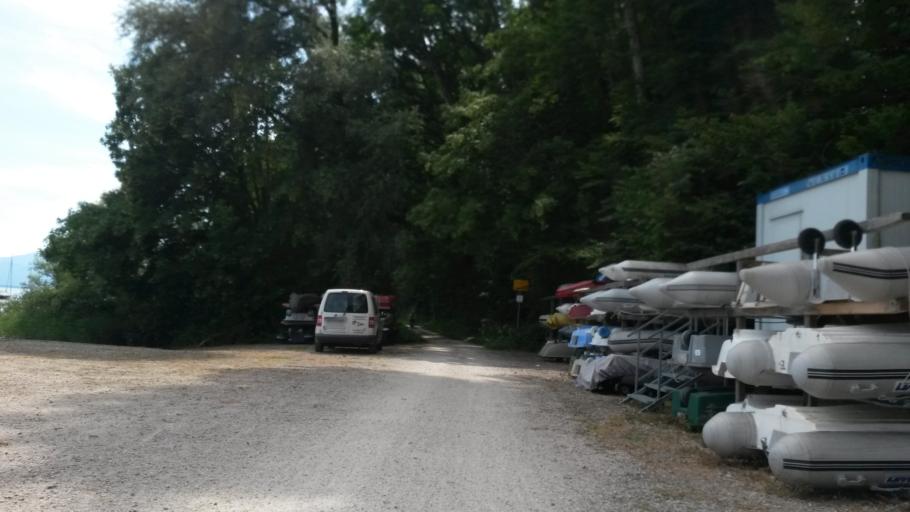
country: DE
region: Bavaria
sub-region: Upper Bavaria
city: Gstadt am Chiemsee
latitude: 47.9104
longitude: 12.4349
